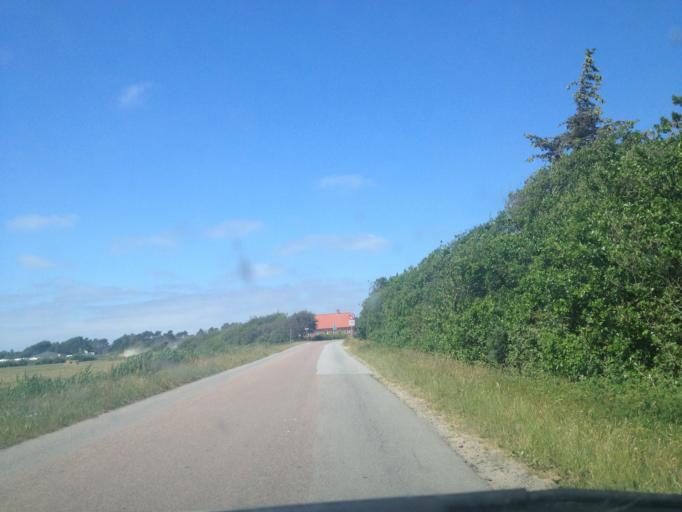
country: DE
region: Schleswig-Holstein
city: List
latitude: 55.0881
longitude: 8.5424
